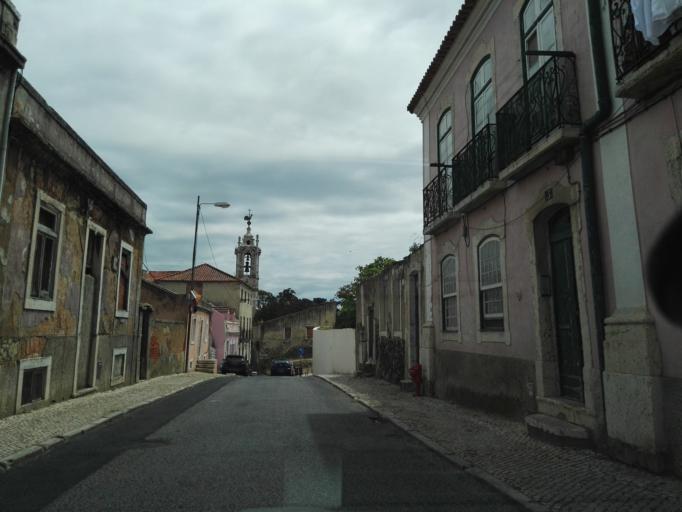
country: PT
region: Lisbon
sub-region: Oeiras
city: Alges
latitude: 38.7098
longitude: -9.1964
